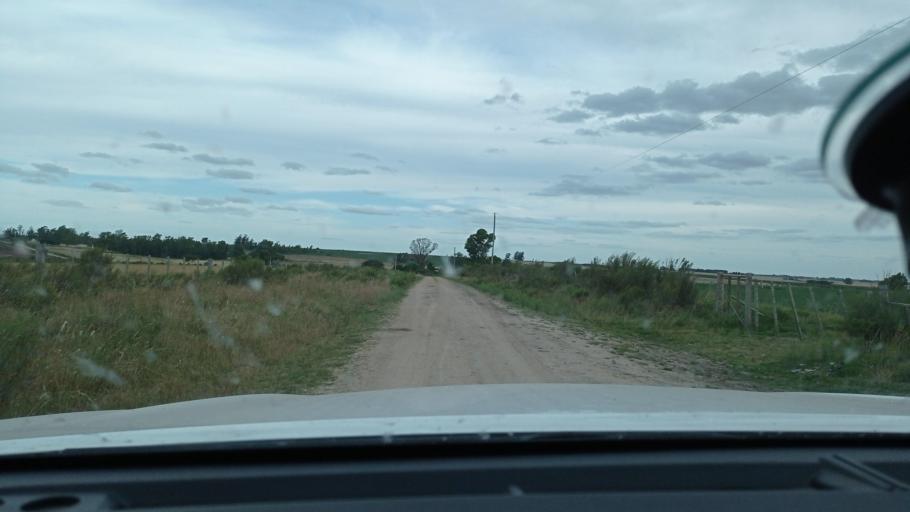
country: UY
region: Florida
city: Casupa
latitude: -34.1156
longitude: -55.8310
